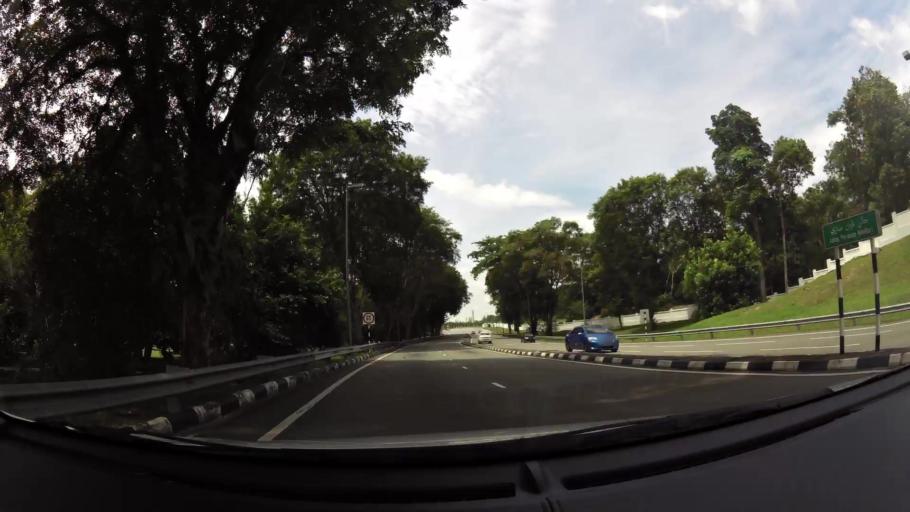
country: BN
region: Brunei and Muara
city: Bandar Seri Begawan
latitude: 4.9166
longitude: 114.9319
